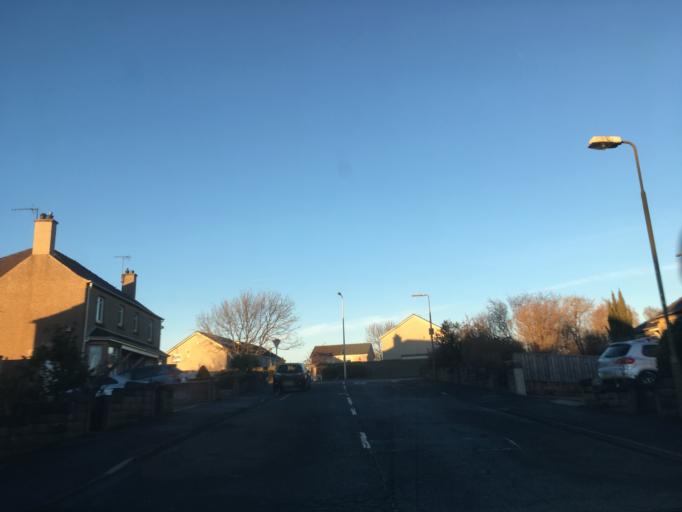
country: GB
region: Scotland
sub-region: Edinburgh
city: Currie
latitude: 55.9448
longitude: -3.3016
